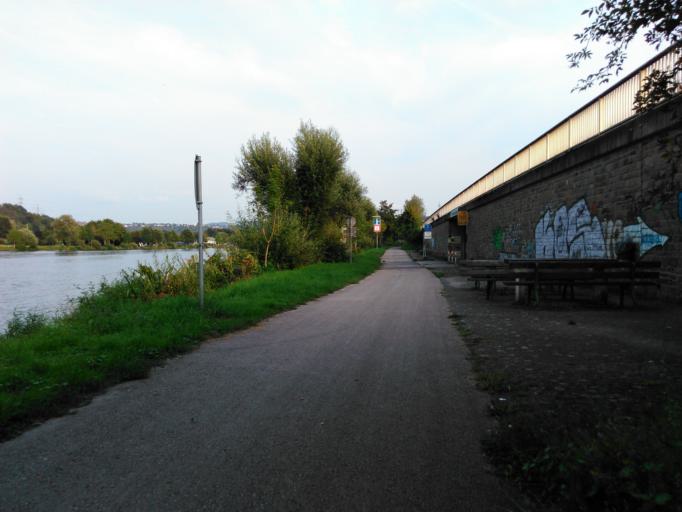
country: DE
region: Rheinland-Pfalz
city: Wasserliesch
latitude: 49.7066
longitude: 6.5470
